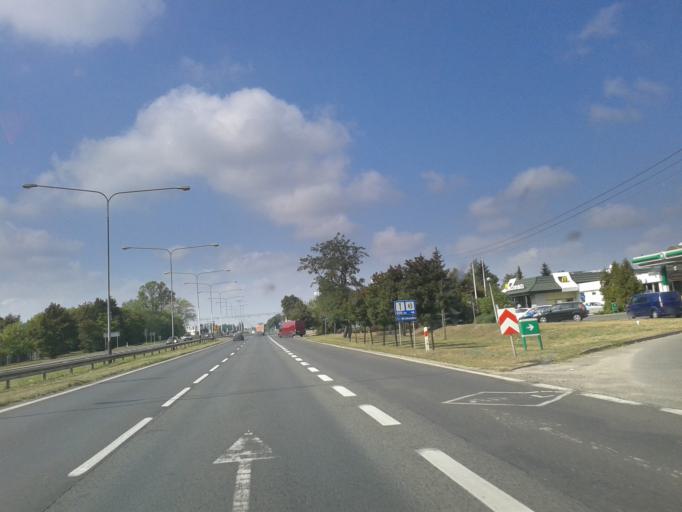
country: PL
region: Greater Poland Voivodeship
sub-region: Powiat poznanski
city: Baranowo
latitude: 52.4331
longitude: 16.8019
